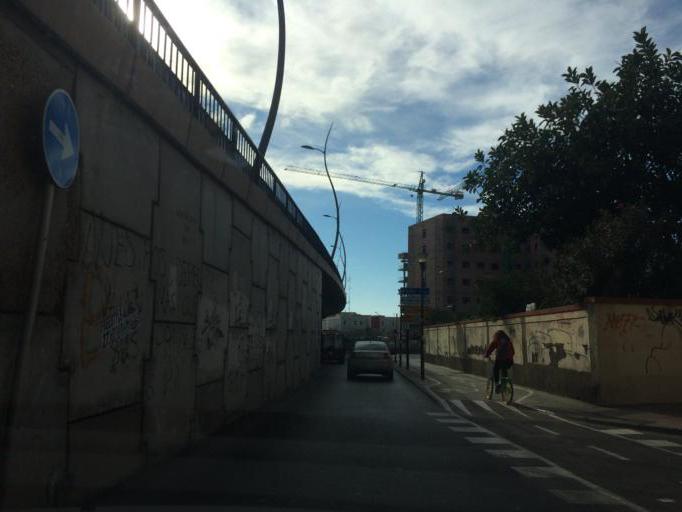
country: ES
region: Andalusia
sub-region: Provincia de Almeria
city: Almeria
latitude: 36.8387
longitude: -2.4476
